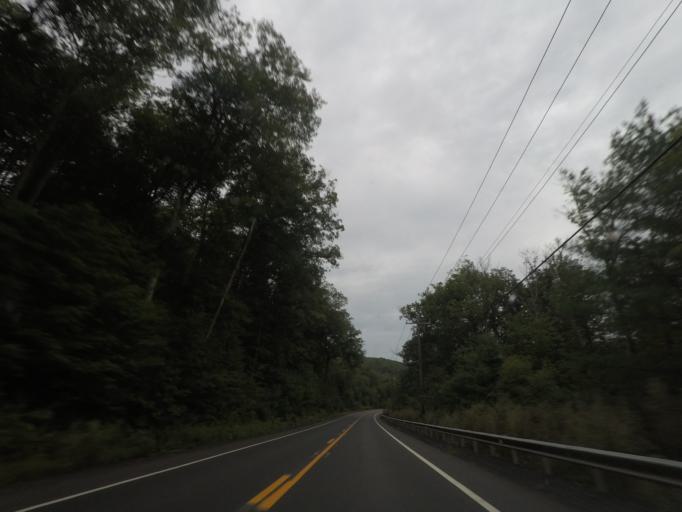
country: US
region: Massachusetts
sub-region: Hampshire County
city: Ware
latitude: 42.1999
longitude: -72.2644
